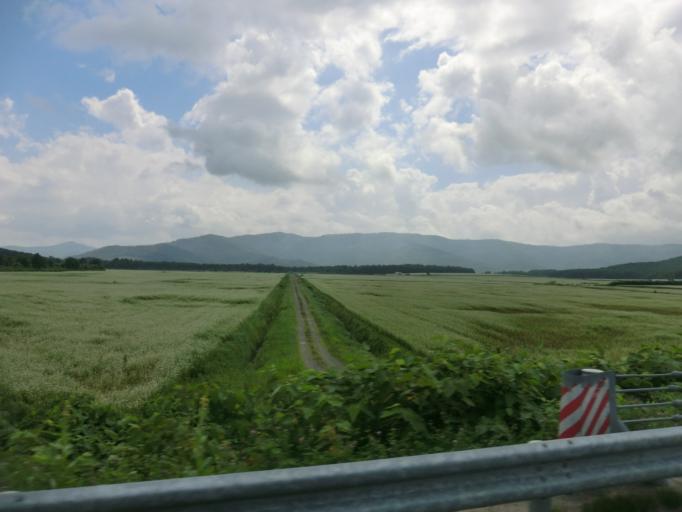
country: JP
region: Hokkaido
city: Fukagawa
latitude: 43.9748
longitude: 142.1437
